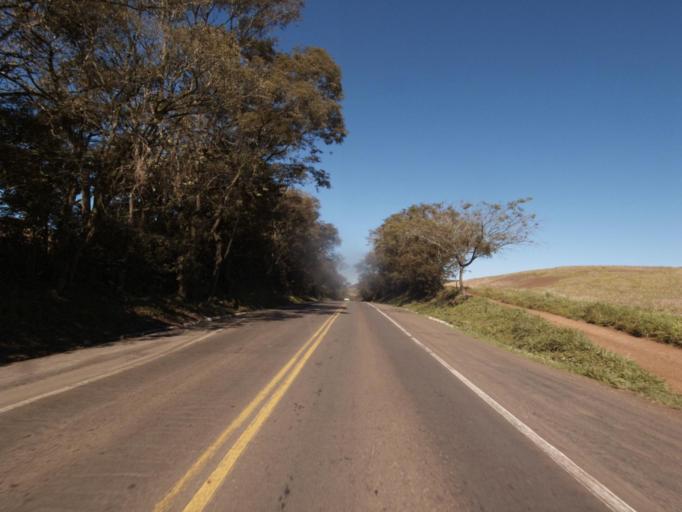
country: BR
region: Rio Grande do Sul
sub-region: Frederico Westphalen
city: Frederico Westphalen
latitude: -26.8110
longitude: -53.3624
